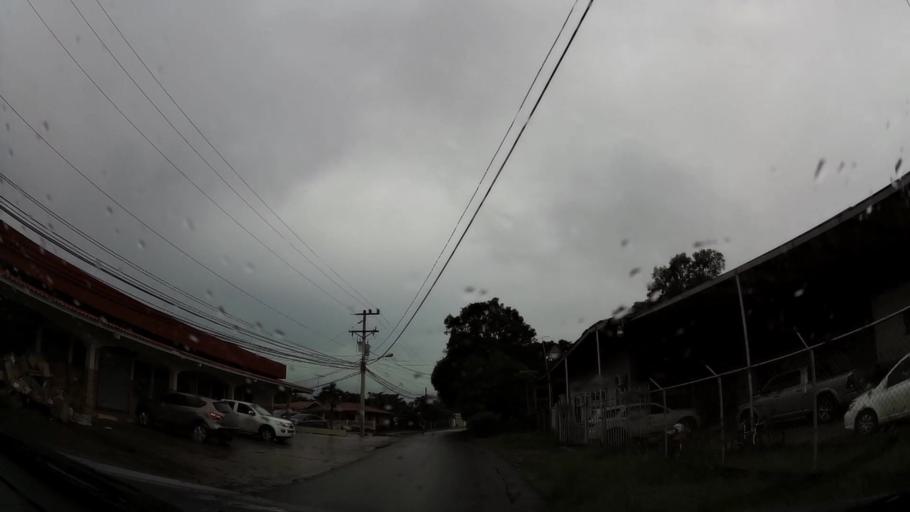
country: PA
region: Veraguas
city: Santiago de Veraguas
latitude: 8.0933
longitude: -80.9550
